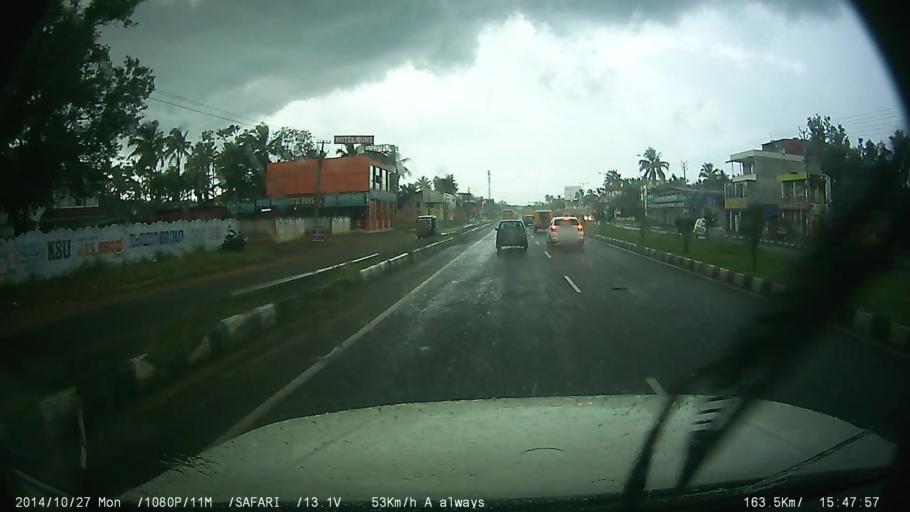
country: IN
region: Kerala
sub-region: Ernakulam
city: Angamali
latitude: 10.2242
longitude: 76.3755
